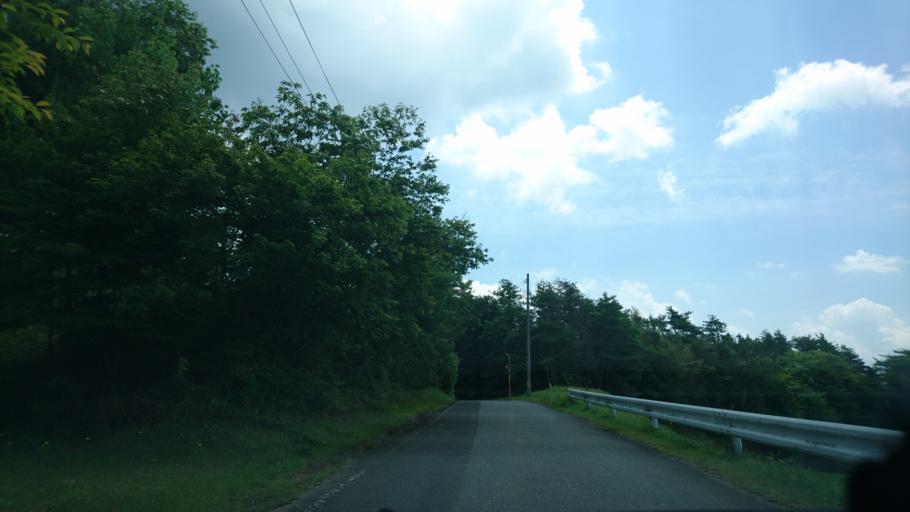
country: JP
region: Iwate
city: Ichinoseki
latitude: 38.9120
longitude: 141.2041
